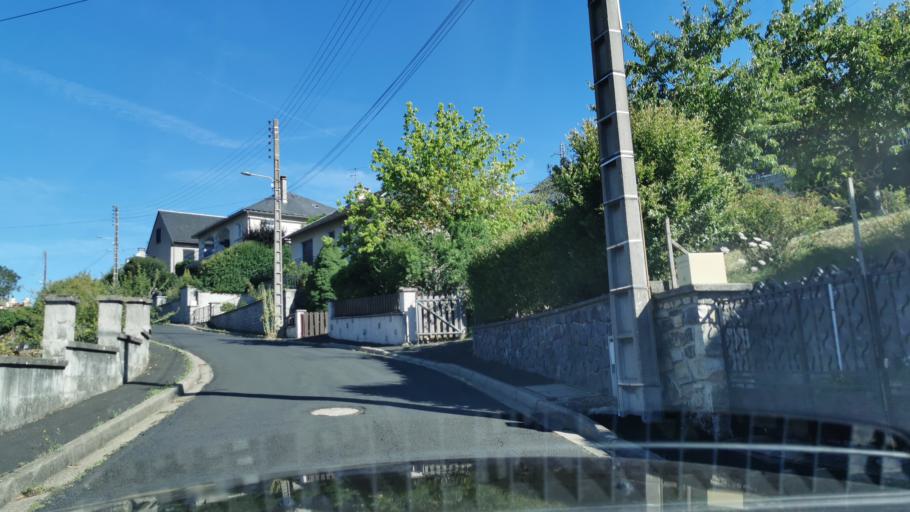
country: FR
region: Auvergne
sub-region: Departement du Cantal
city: Saint-Flour
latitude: 45.0373
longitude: 3.1068
